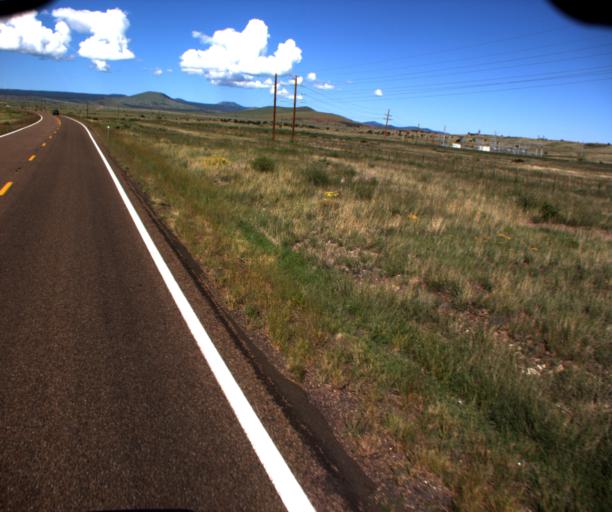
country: US
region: Arizona
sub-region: Apache County
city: Eagar
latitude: 34.1075
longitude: -109.3387
